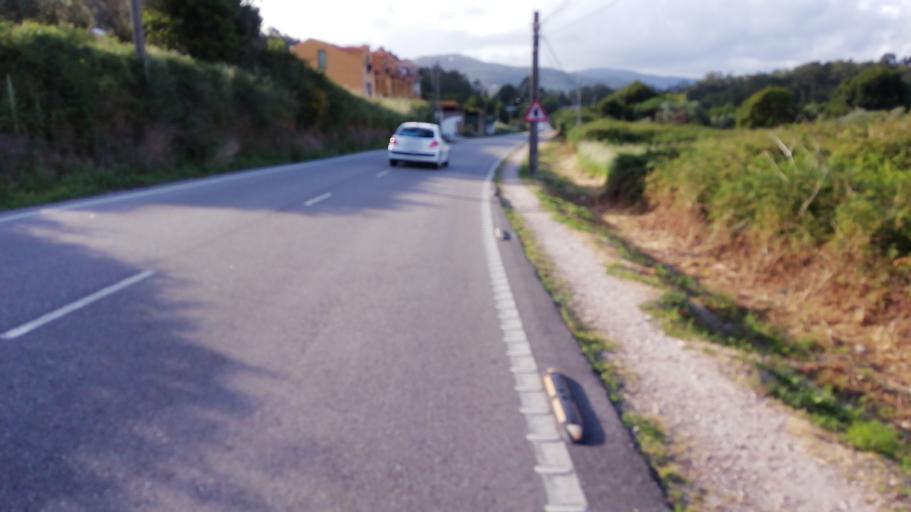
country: ES
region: Galicia
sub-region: Provincia de Pontevedra
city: A Guarda
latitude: 41.8915
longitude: -8.8582
